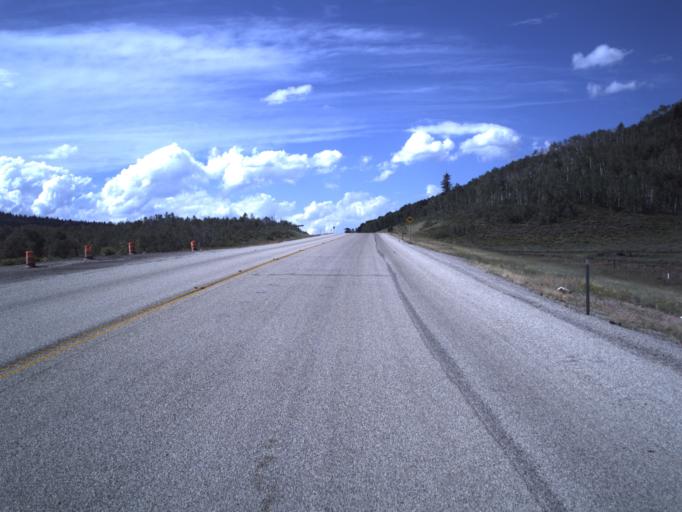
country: US
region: Utah
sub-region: Wasatch County
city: Heber
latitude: 40.2938
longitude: -111.2504
